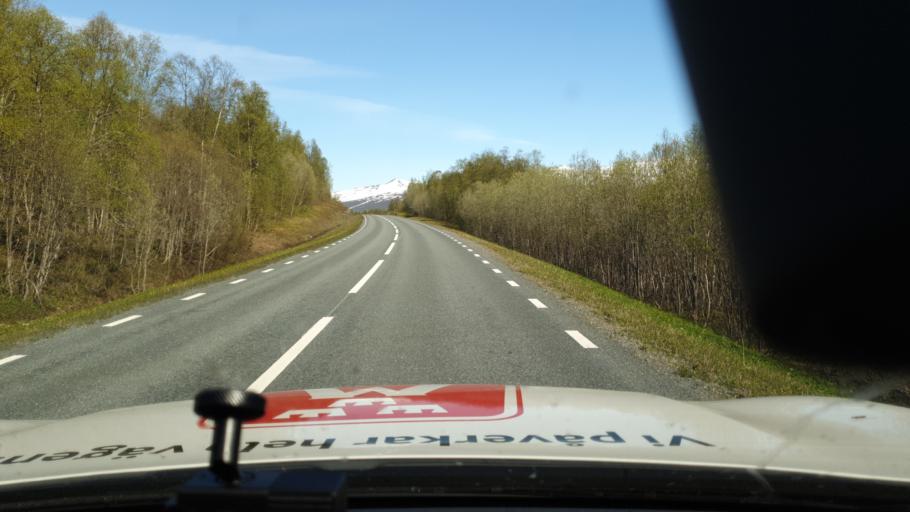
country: NO
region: Nordland
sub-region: Rana
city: Mo i Rana
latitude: 65.7613
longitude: 15.1163
